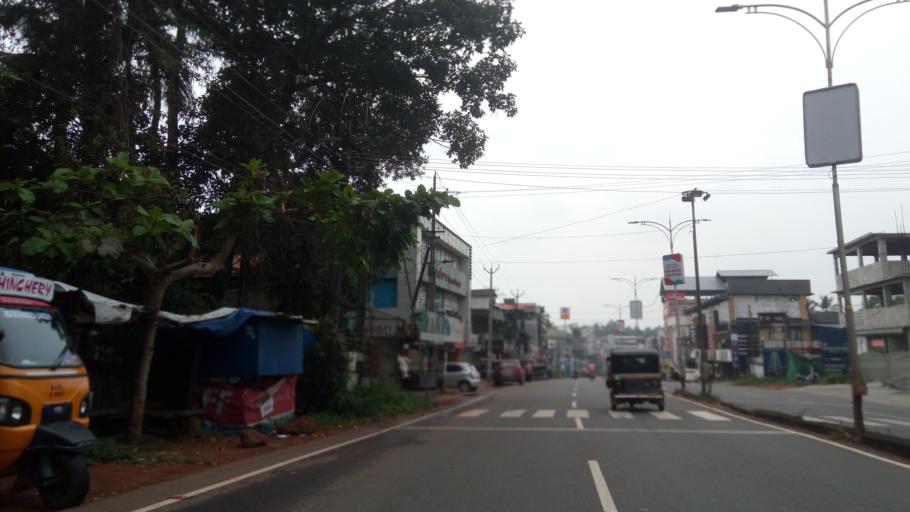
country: IN
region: Kerala
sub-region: Malappuram
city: Malappuram
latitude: 10.9999
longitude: 75.9982
